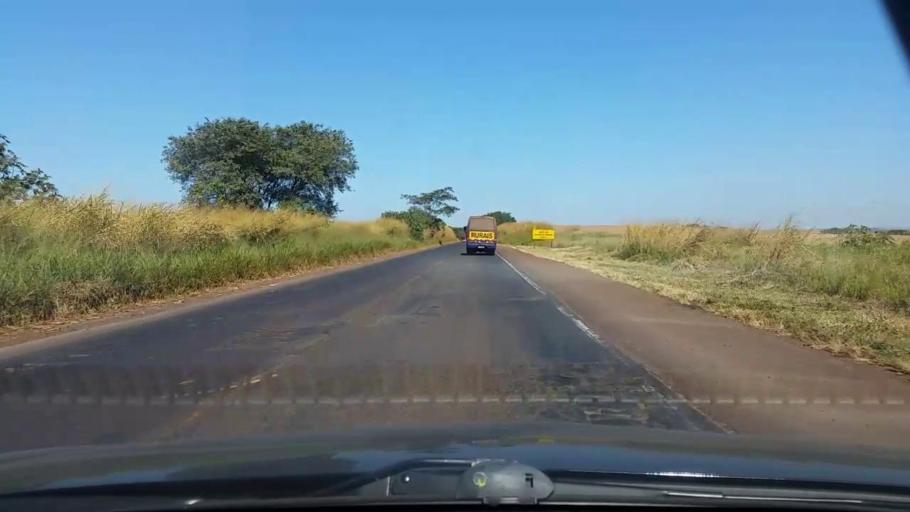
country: BR
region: Sao Paulo
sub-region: Igaracu Do Tiete
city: Igaracu do Tiete
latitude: -22.5675
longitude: -48.5638
